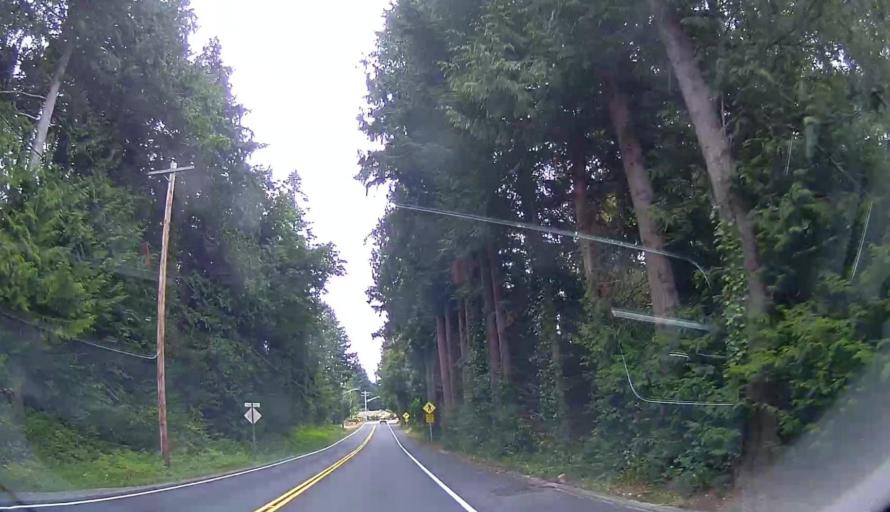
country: US
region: Washington
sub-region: Snohomish County
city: Warm Beach
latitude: 48.1797
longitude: -122.3519
